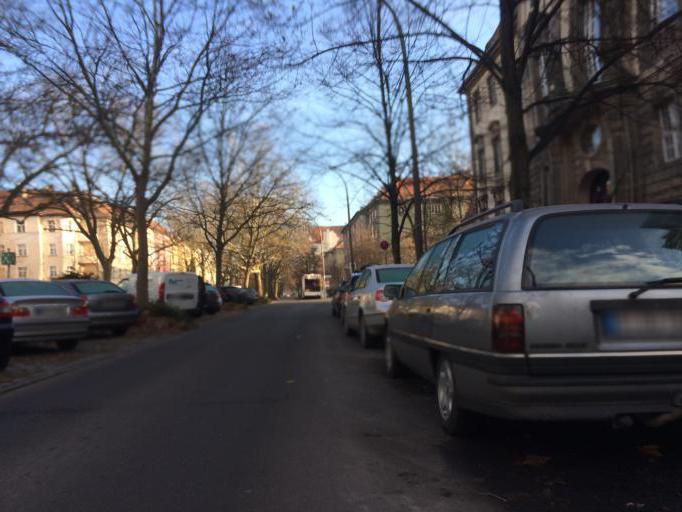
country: DE
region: Berlin
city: Pankow
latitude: 52.5664
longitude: 13.4152
